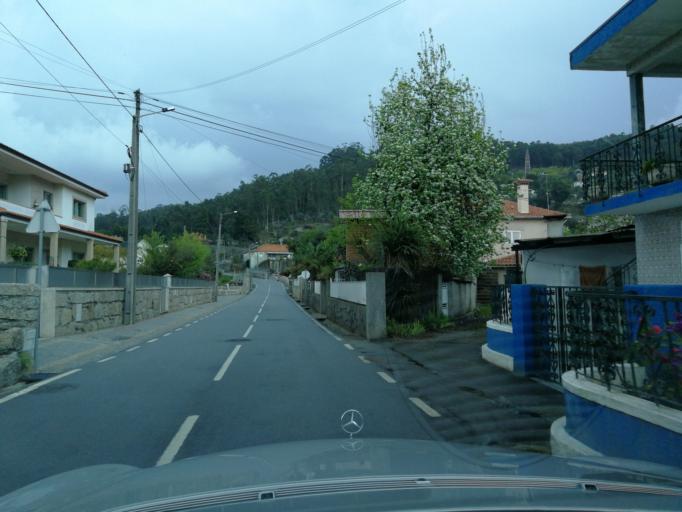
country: PT
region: Braga
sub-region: Braga
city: Oliveira
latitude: 41.4682
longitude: -8.4781
